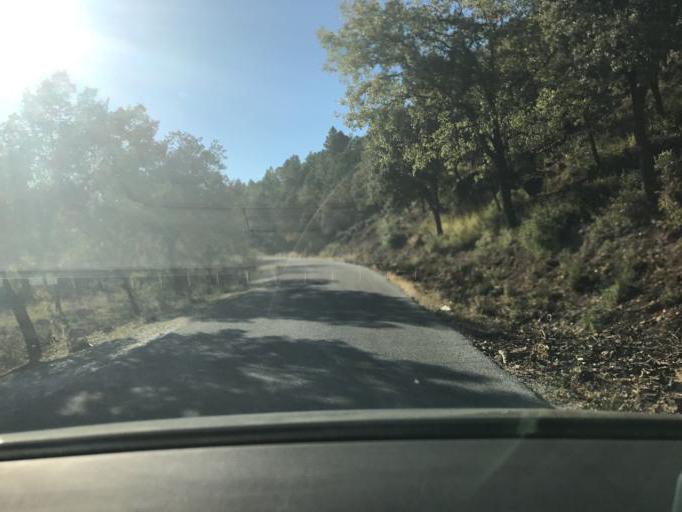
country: ES
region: Andalusia
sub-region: Provincia de Granada
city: Beas de Granada
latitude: 37.2951
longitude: -3.4793
